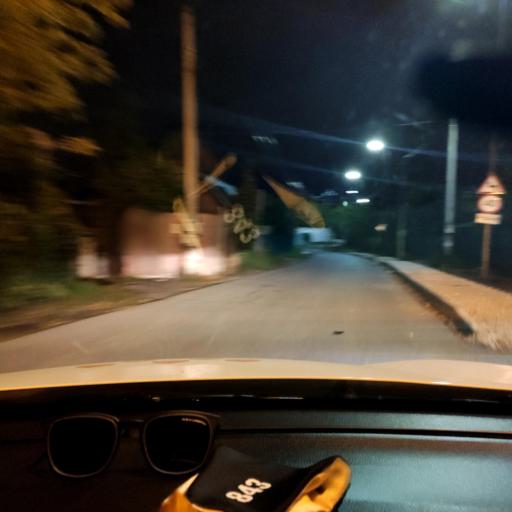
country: RU
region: Tatarstan
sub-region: Gorod Kazan'
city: Kazan
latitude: 55.7401
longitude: 49.1649
